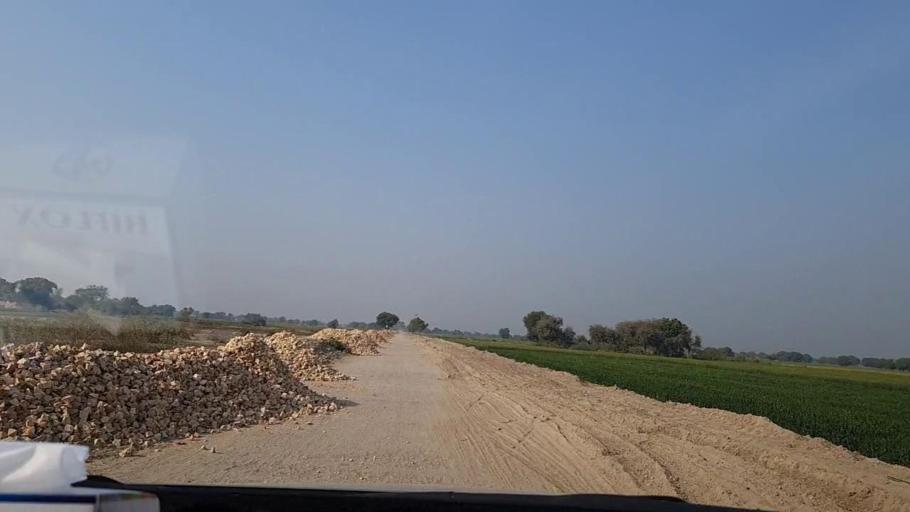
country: PK
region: Sindh
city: Tando Ghulam Ali
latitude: 25.1689
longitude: 68.8780
